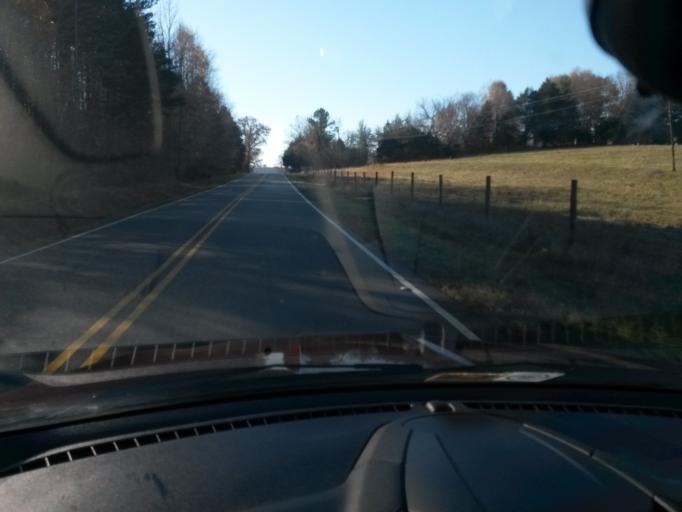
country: US
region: Virginia
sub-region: Charlotte County
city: Charlotte Court House
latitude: 37.1024
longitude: -78.6429
